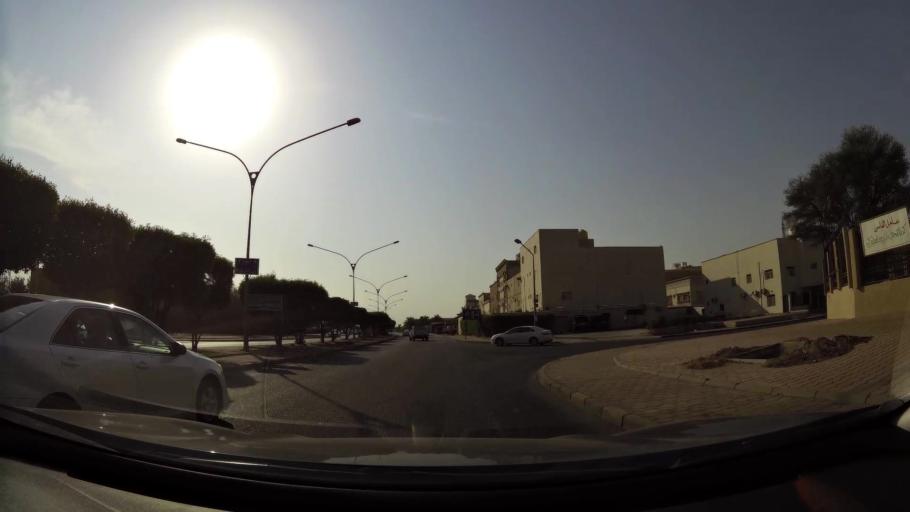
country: KW
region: Mubarak al Kabir
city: Mubarak al Kabir
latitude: 29.1691
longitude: 48.0620
